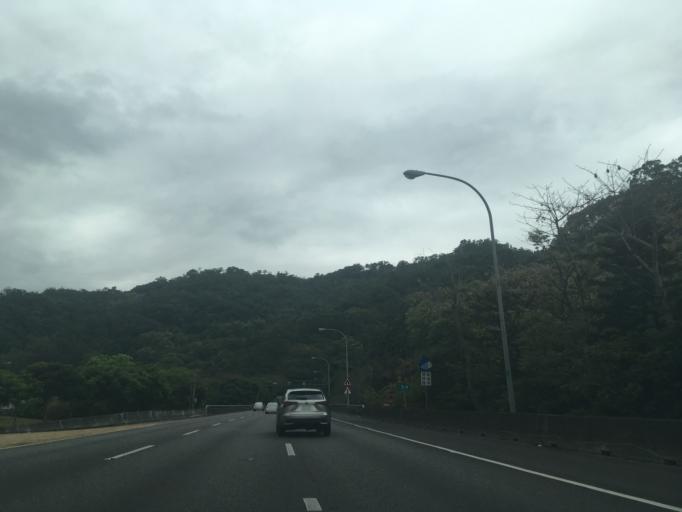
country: TW
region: Taipei
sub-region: Taipei
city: Banqiao
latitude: 24.9795
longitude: 121.5006
